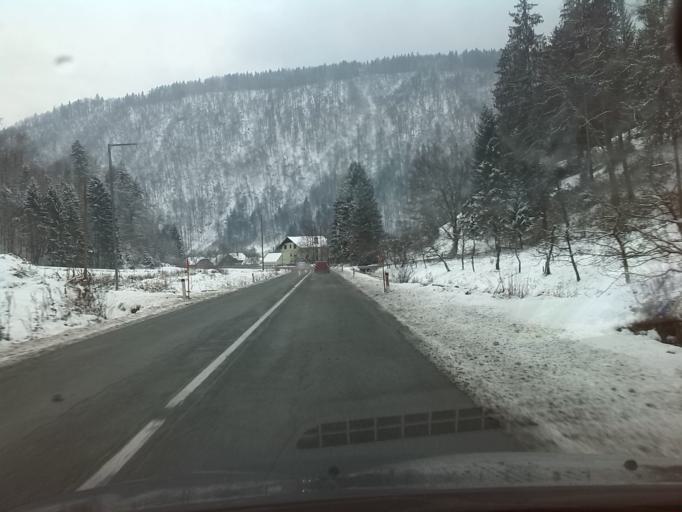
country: SI
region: Kamnik
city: Mekinje
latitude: 46.2311
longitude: 14.6673
